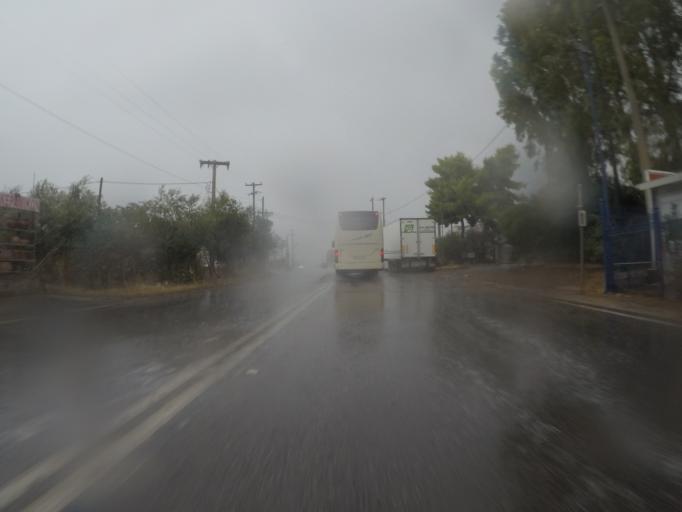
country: GR
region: Peloponnese
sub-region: Nomos Messinias
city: Sperkhoyia
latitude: 37.0455
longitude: 22.0825
